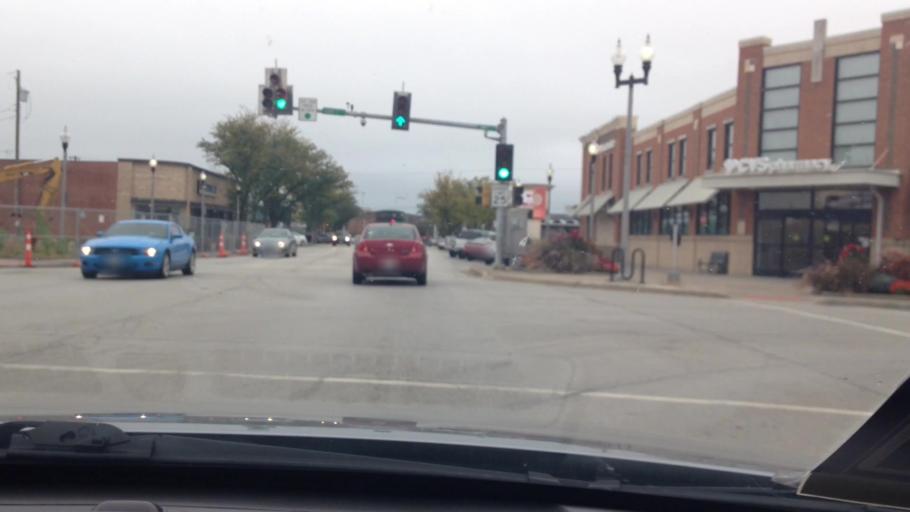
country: US
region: Missouri
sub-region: Clay County
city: North Kansas City
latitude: 39.1420
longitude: -94.5771
